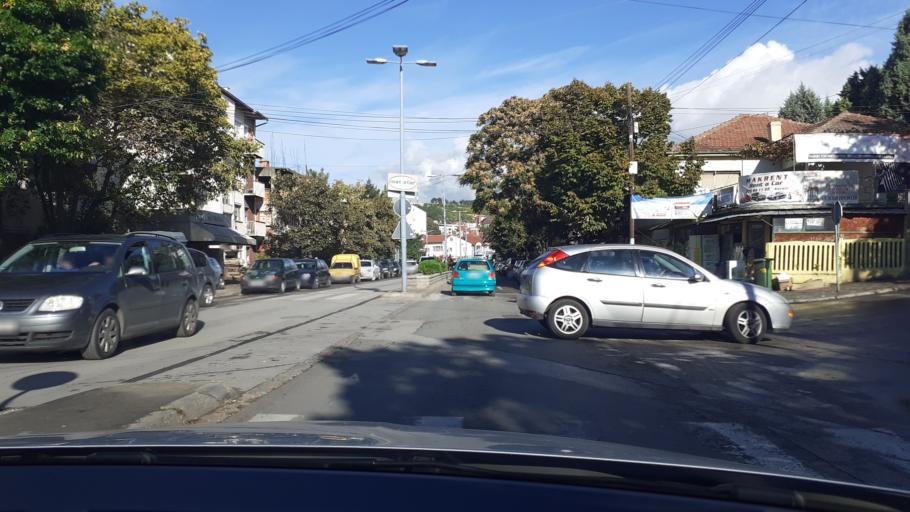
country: MK
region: Kocani
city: Kochani
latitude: 41.9136
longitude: 22.4149
